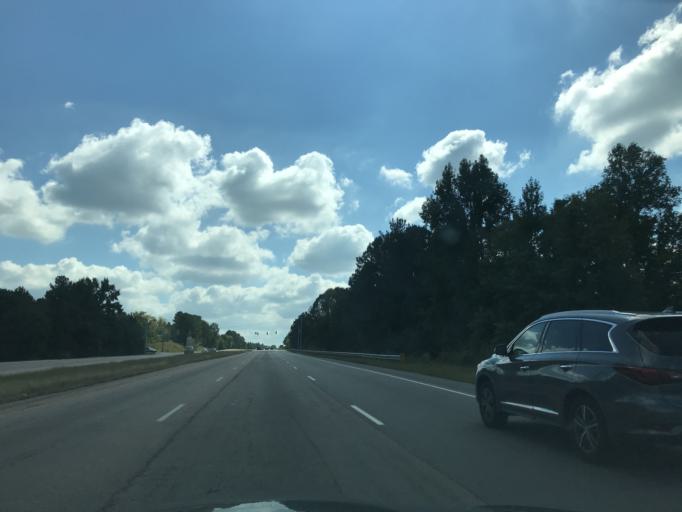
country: US
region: North Carolina
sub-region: Wake County
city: Wake Forest
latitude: 35.9568
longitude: -78.5416
